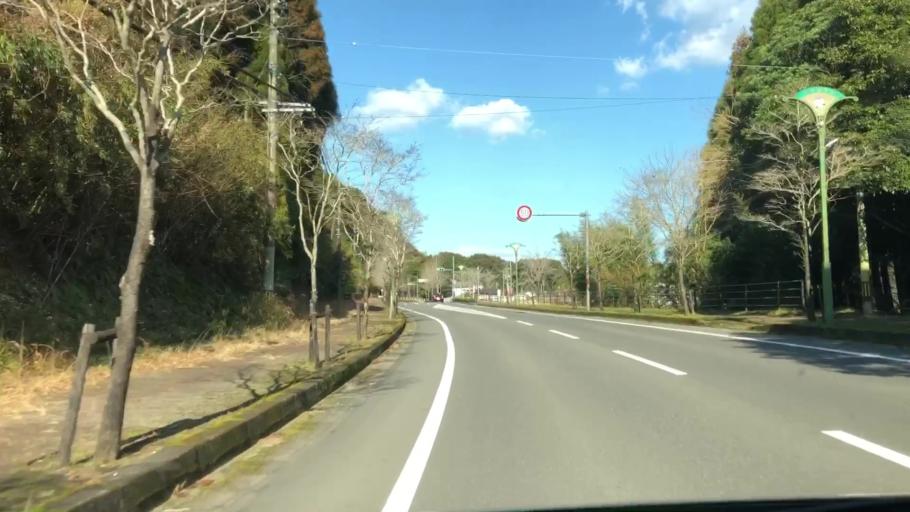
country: JP
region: Kagoshima
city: Satsumasendai
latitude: 31.8257
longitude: 130.4345
